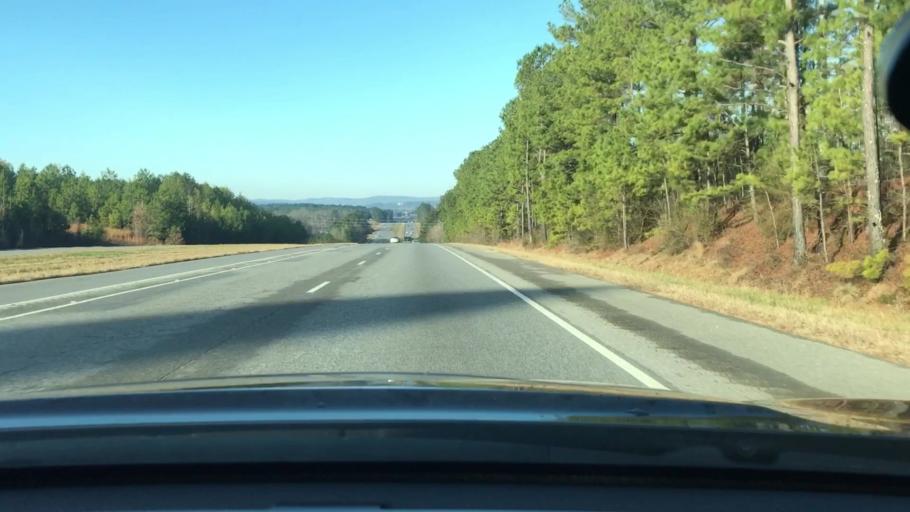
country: US
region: Alabama
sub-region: Shelby County
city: Chelsea
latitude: 33.3503
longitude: -86.5867
